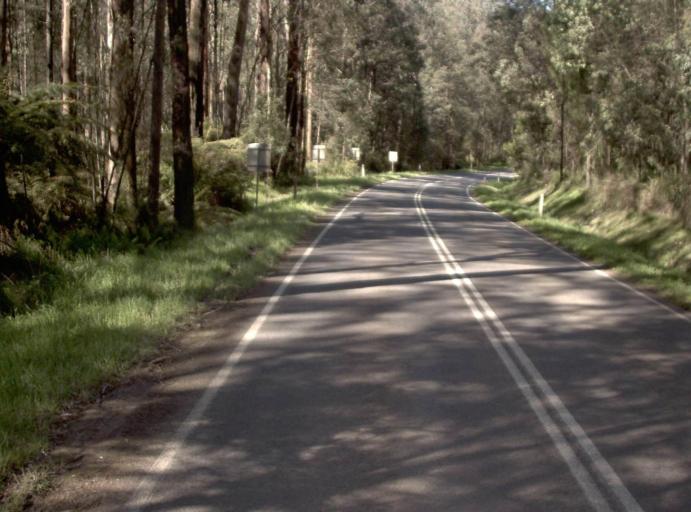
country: AU
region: Victoria
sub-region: Yarra Ranges
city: Millgrove
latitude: -37.8819
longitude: 145.8610
